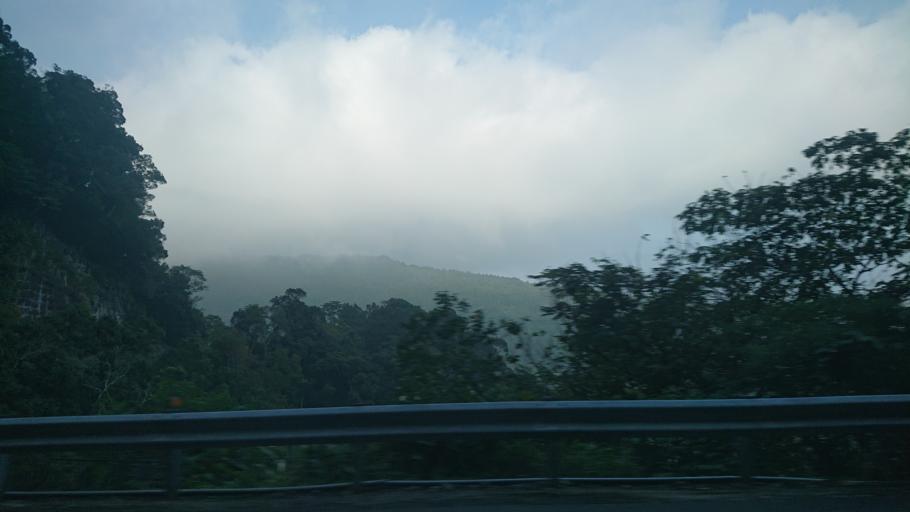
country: TW
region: Taiwan
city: Lugu
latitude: 23.4777
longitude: 120.7352
